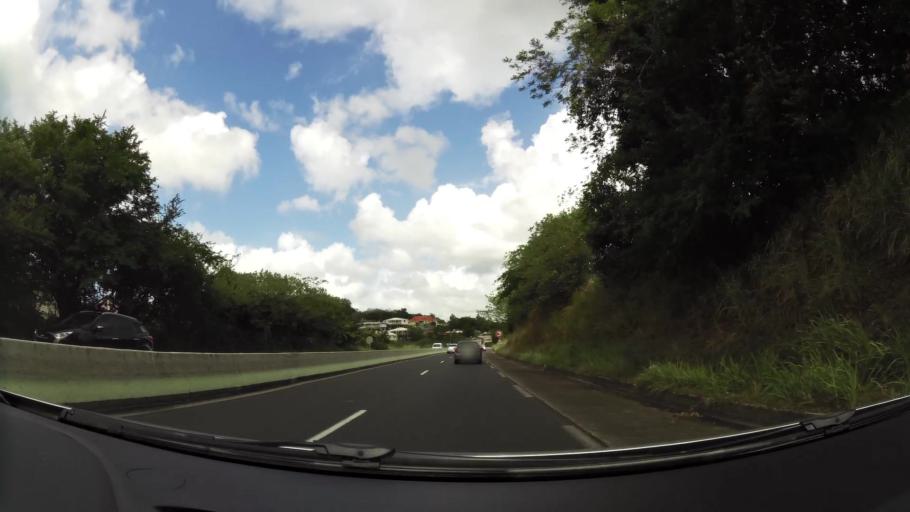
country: MQ
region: Martinique
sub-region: Martinique
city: Les Trois-Ilets
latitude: 14.5147
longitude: -60.9830
